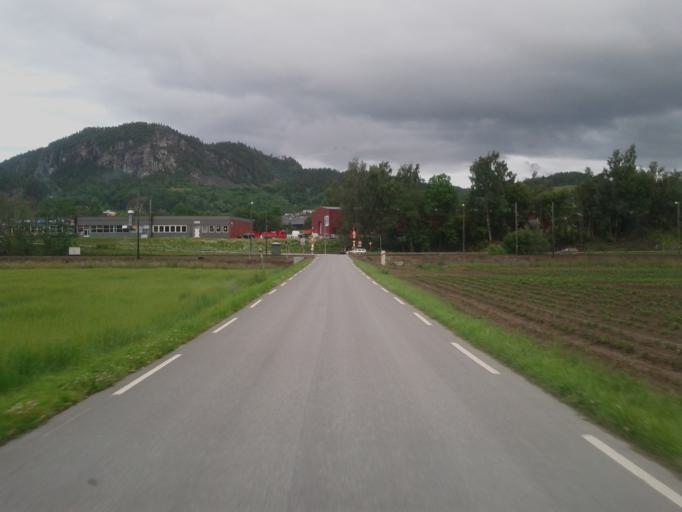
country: NO
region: Sor-Trondelag
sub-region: Melhus
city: Lundamo
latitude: 63.1506
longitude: 10.2717
